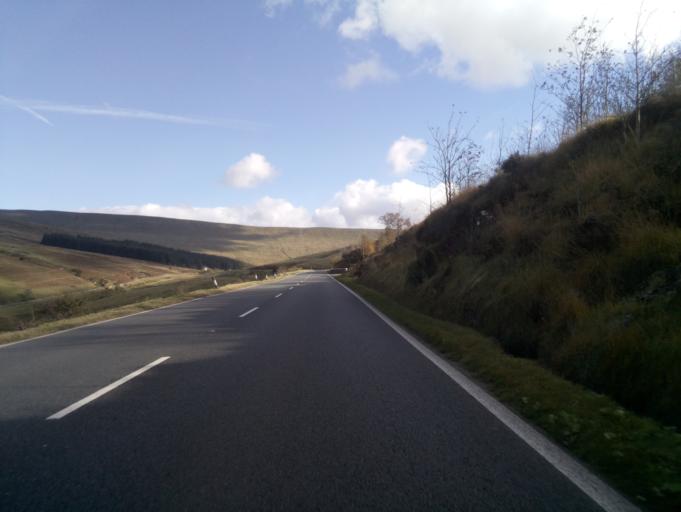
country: GB
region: Wales
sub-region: Sir Powys
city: Brecon
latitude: 51.8744
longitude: -3.4919
